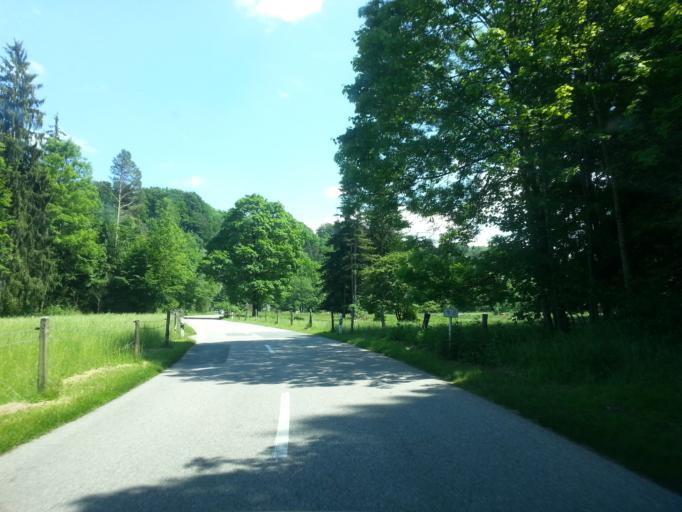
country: DE
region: Bavaria
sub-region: Upper Bavaria
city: Irschenberg
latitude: 47.8290
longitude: 11.8817
